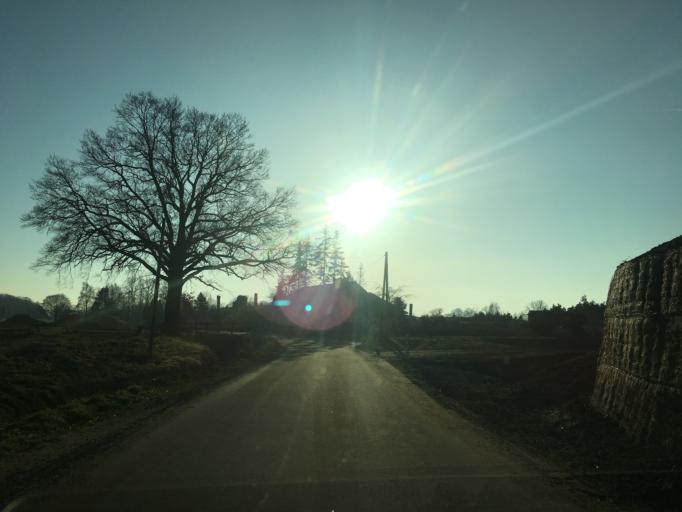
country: DE
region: North Rhine-Westphalia
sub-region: Regierungsbezirk Munster
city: Nordwalde
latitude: 52.0786
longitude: 7.4862
